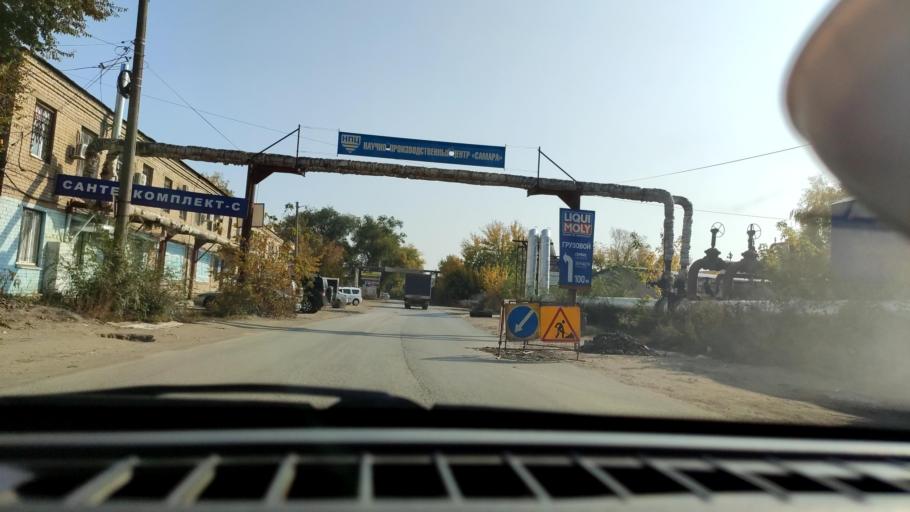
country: RU
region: Samara
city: Samara
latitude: 53.1958
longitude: 50.2603
